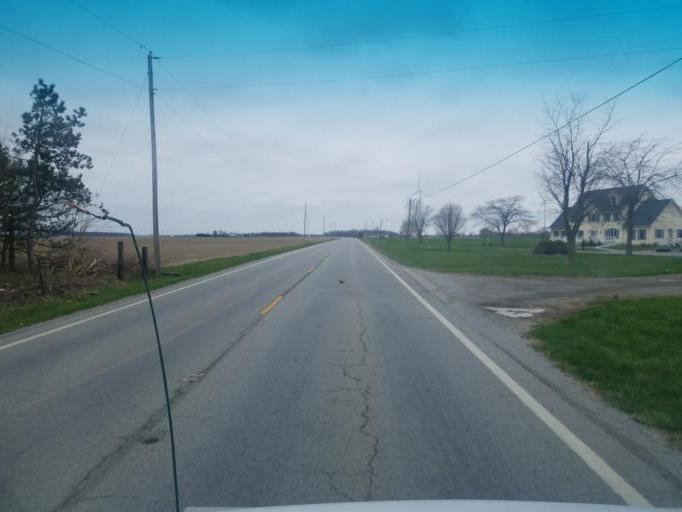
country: US
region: Ohio
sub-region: Van Wert County
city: Van Wert
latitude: 40.9242
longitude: -84.5393
